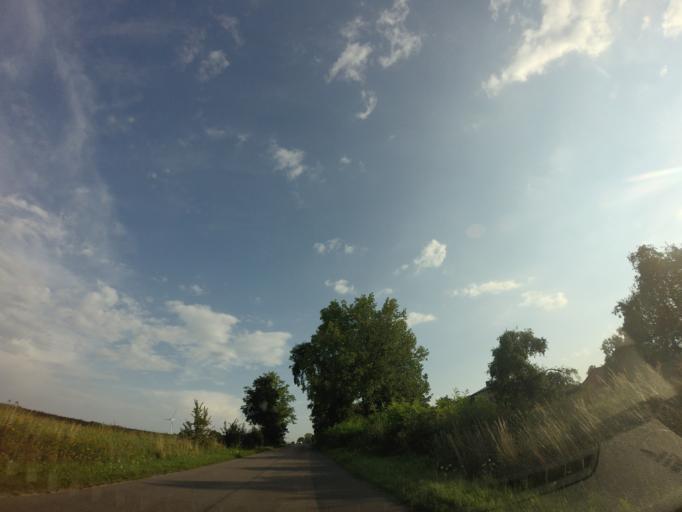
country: PL
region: Lublin Voivodeship
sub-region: Powiat lubartowski
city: Michow
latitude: 51.5151
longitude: 22.3105
